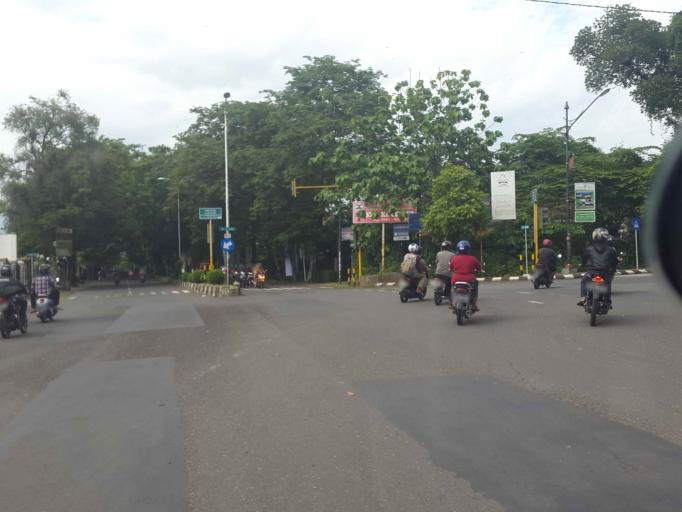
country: ID
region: Central Java
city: Purwokerto
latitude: -7.4165
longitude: 109.2305
